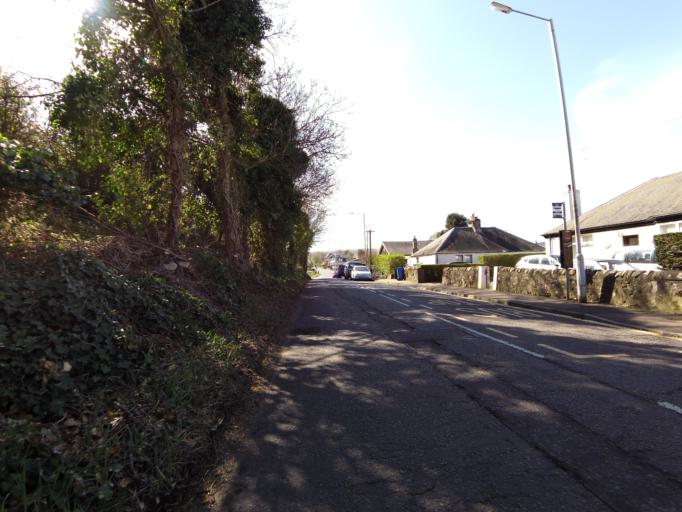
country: GB
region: Scotland
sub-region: Dundee City
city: Dundee
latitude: 56.4217
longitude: -2.9818
